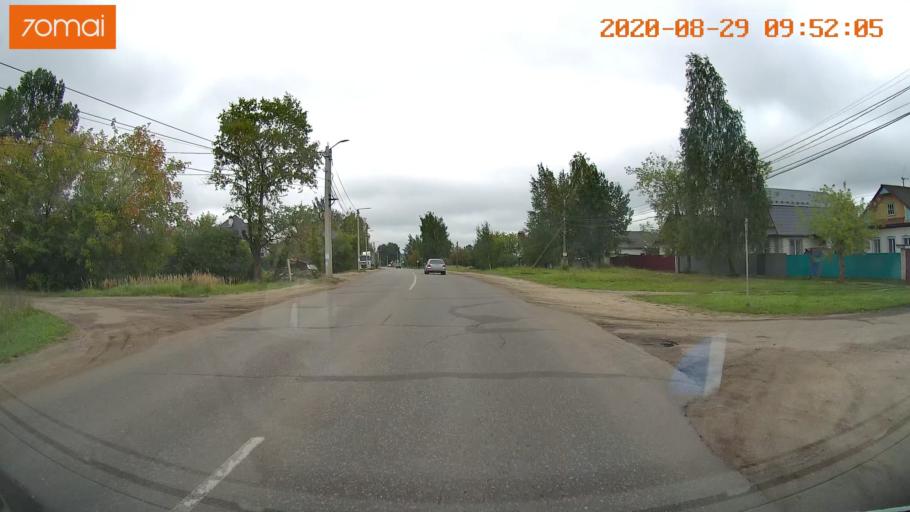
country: RU
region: Ivanovo
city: Kineshma
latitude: 57.4255
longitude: 42.2052
